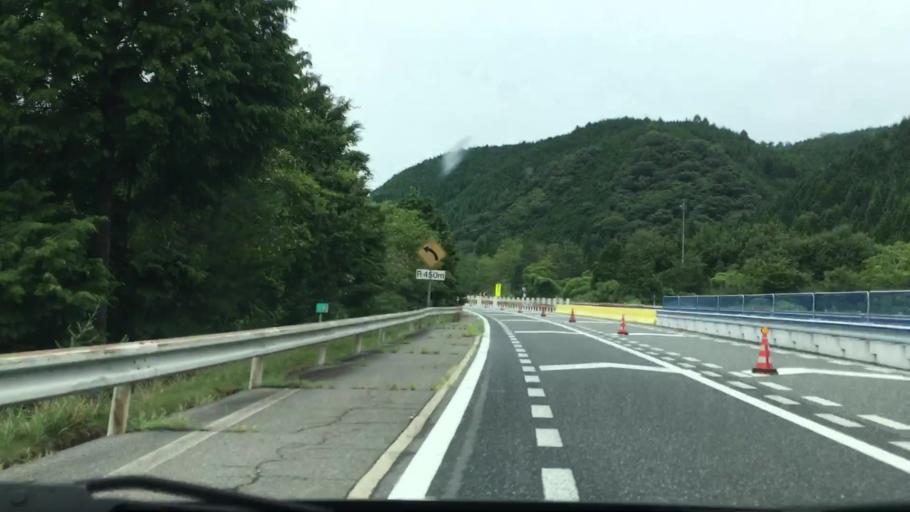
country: JP
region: Okayama
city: Niimi
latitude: 35.0345
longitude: 133.5737
